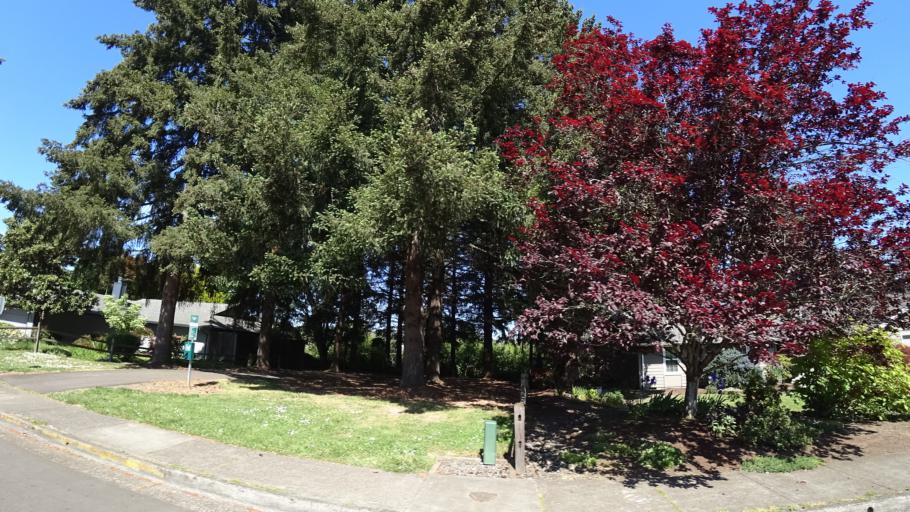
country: US
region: Oregon
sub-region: Washington County
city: Beaverton
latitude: 45.4559
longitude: -122.7973
